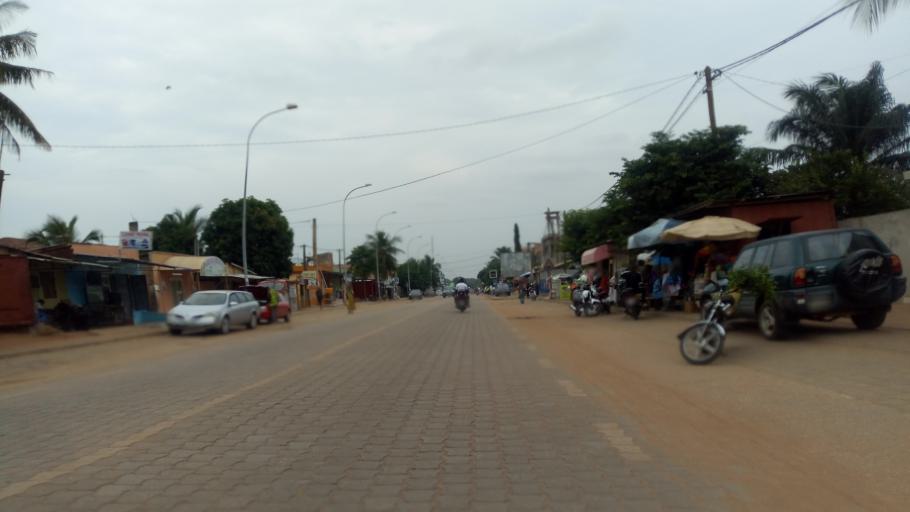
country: TG
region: Maritime
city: Lome
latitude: 6.1824
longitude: 1.1986
